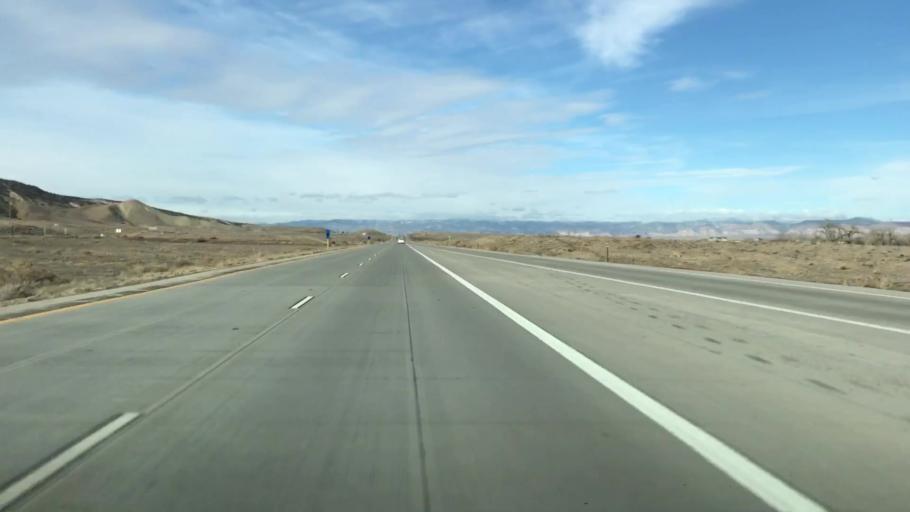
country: US
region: Colorado
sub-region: Mesa County
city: Loma
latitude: 39.1826
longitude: -108.8280
